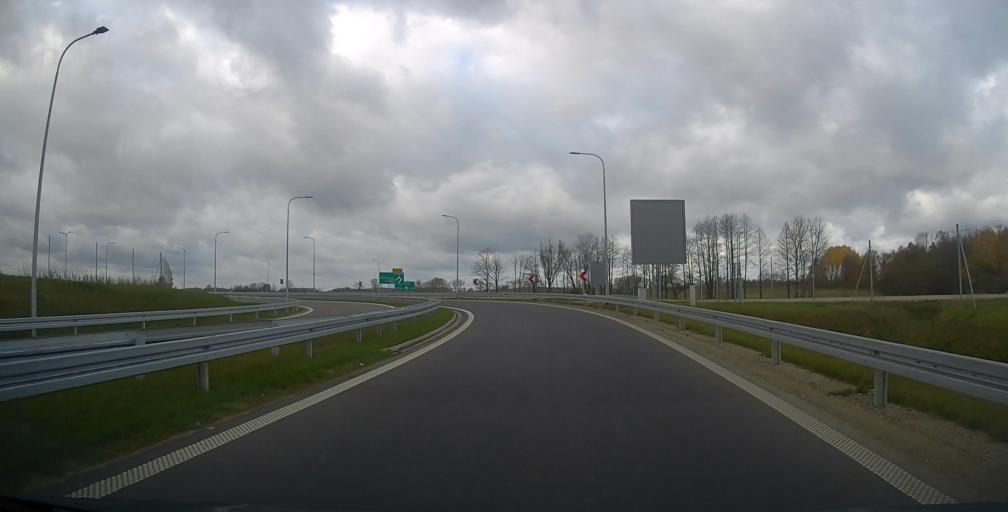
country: PL
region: Podlasie
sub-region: Powiat grajewski
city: Rajgrod
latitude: 53.8588
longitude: 22.5848
